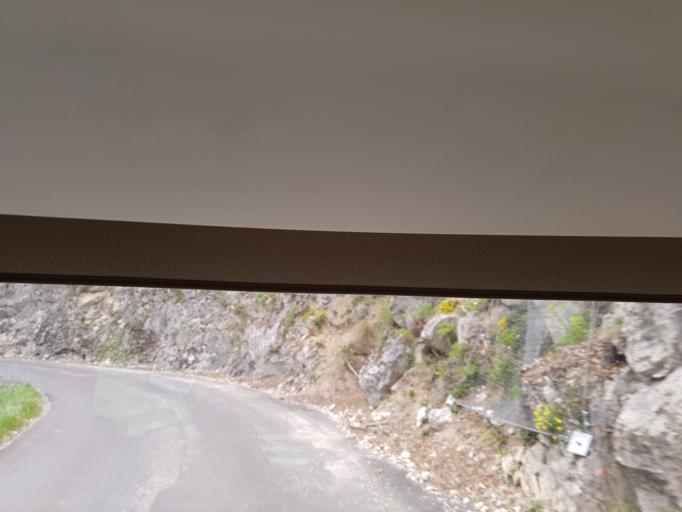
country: FR
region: Languedoc-Roussillon
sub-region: Departement de l'Aude
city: Quillan
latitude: 42.7745
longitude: 2.1758
